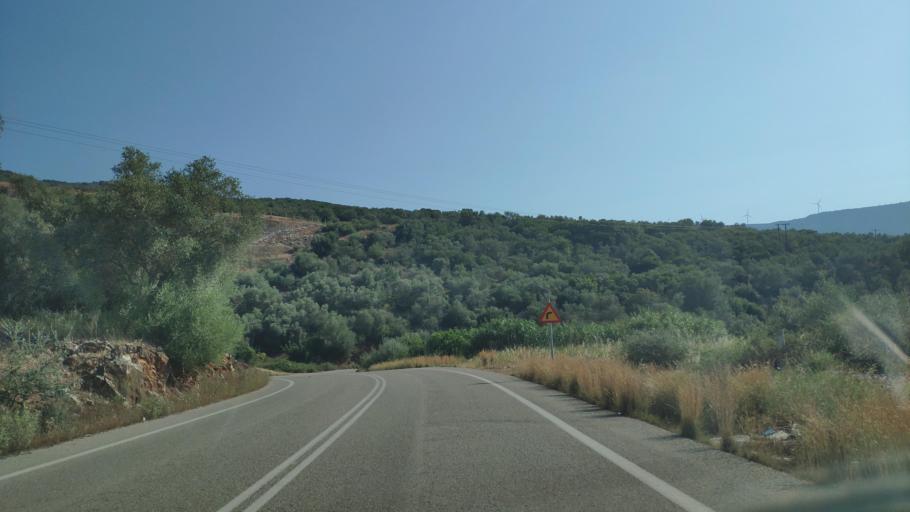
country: GR
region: West Greece
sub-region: Nomos Aitolias kai Akarnanias
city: Stanos
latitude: 38.7696
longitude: 21.1631
